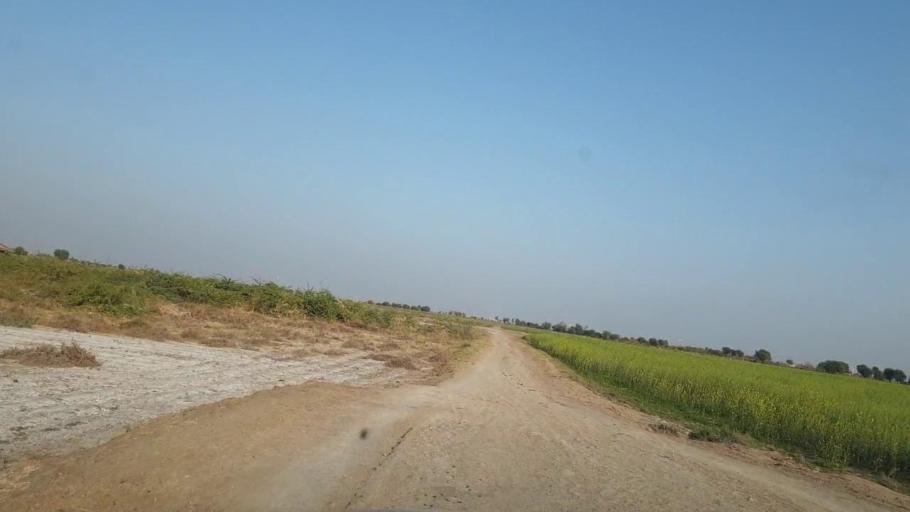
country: PK
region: Sindh
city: Tando Mittha Khan
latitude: 25.7487
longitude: 69.2403
